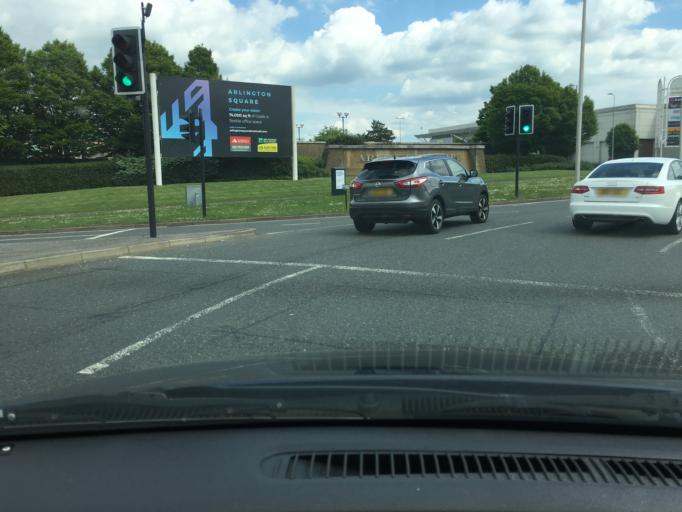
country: GB
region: England
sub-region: Bracknell Forest
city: Bracknell
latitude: 51.4144
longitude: -0.7604
